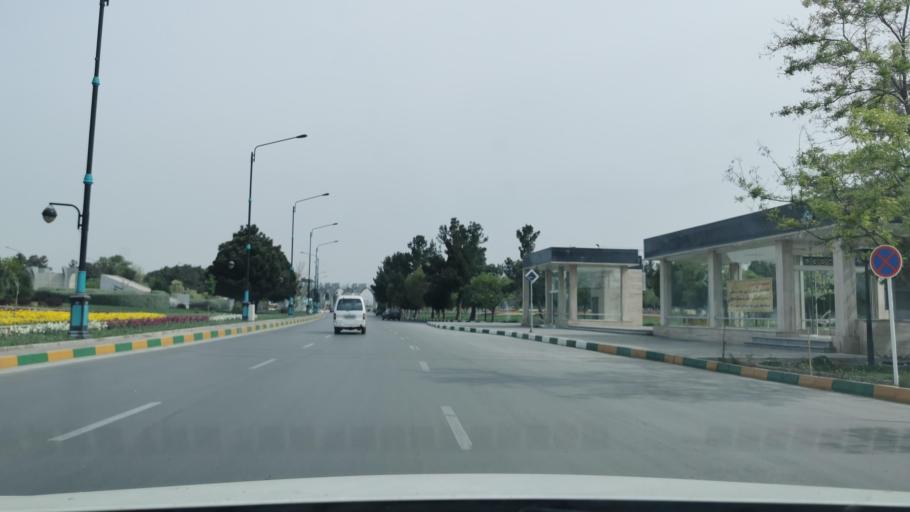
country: IR
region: Razavi Khorasan
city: Mashhad
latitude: 36.2434
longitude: 59.6228
